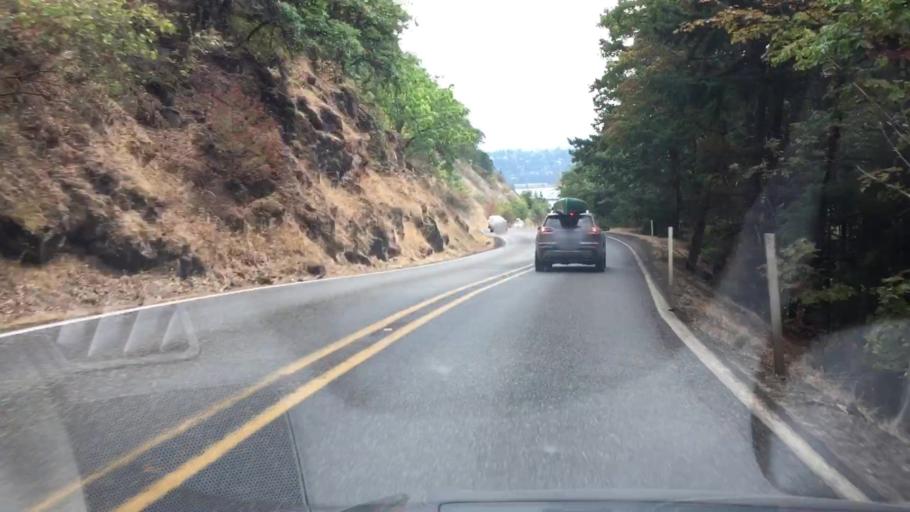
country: US
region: Oregon
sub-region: Hood River County
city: Hood River
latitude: 45.7393
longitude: -121.5217
